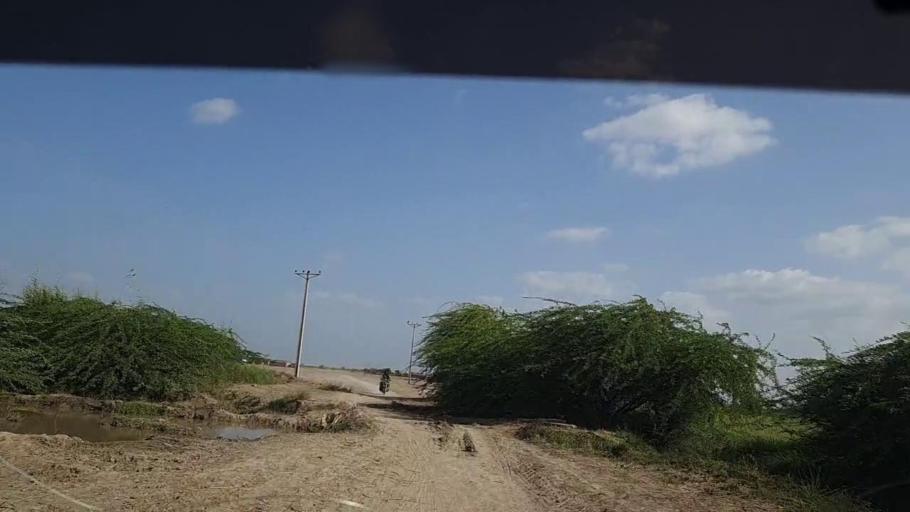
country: PK
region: Sindh
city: Kadhan
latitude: 24.4610
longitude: 68.8538
